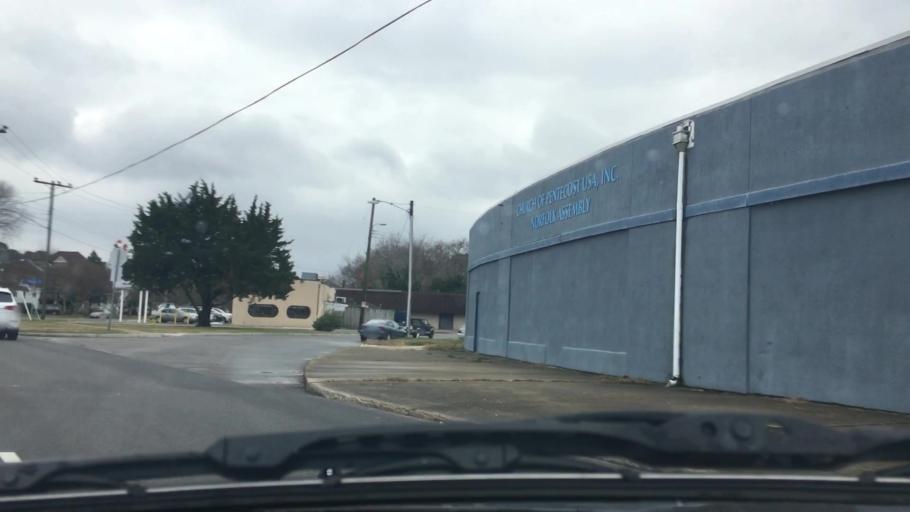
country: US
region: Virginia
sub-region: City of Norfolk
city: Norfolk
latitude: 36.8751
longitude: -76.2539
